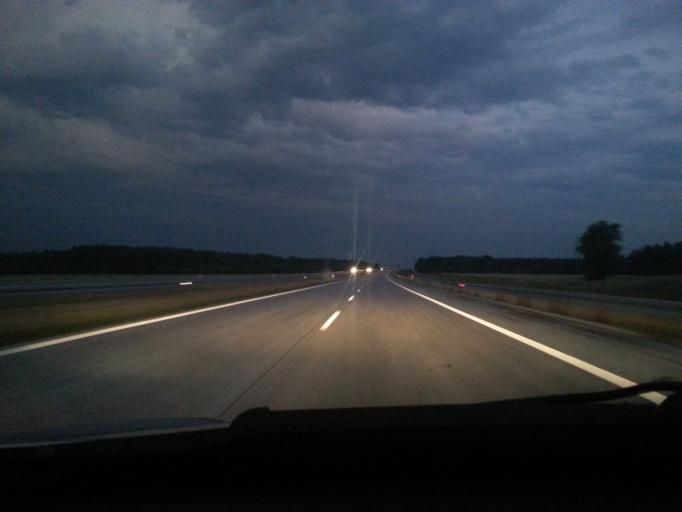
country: PL
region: Lodz Voivodeship
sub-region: Powiat sieradzki
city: Brzeznio
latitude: 51.5161
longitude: 18.6938
